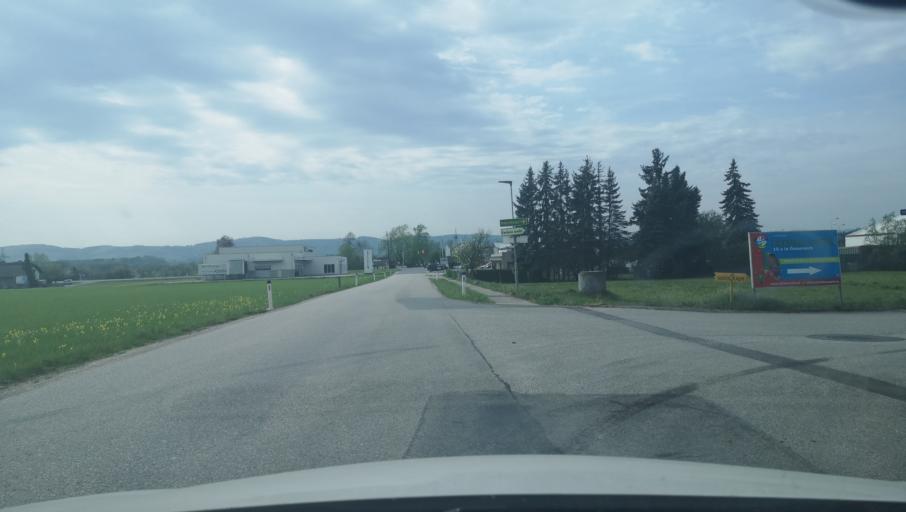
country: AT
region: Lower Austria
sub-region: Politischer Bezirk Amstetten
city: Sankt Georgen am Ybbsfelde
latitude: 48.1156
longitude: 14.9258
